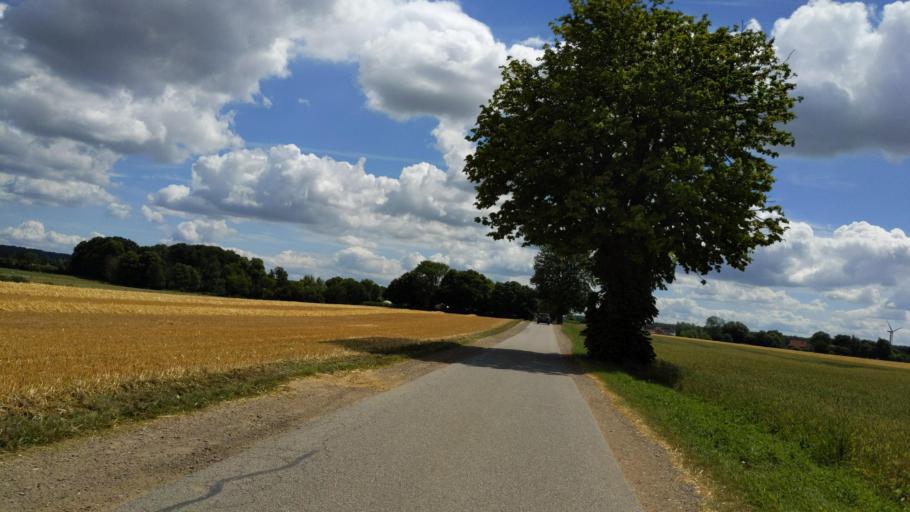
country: DE
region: Mecklenburg-Vorpommern
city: Kalkhorst
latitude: 53.9599
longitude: 11.0129
